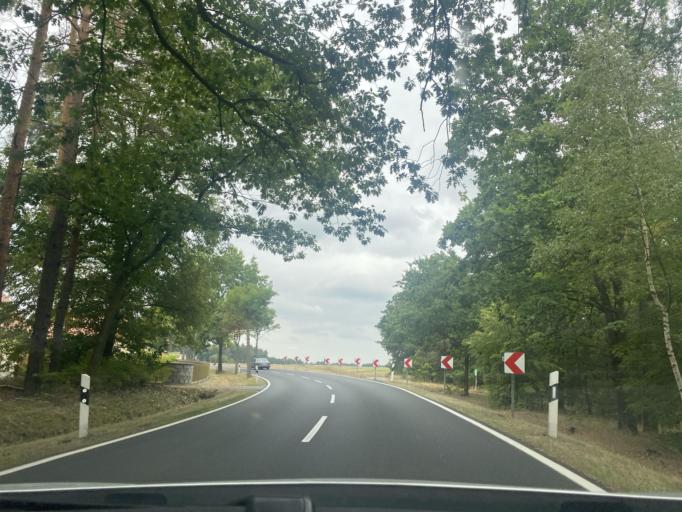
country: DE
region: Saxony
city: Mucka
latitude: 51.2814
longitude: 14.6432
